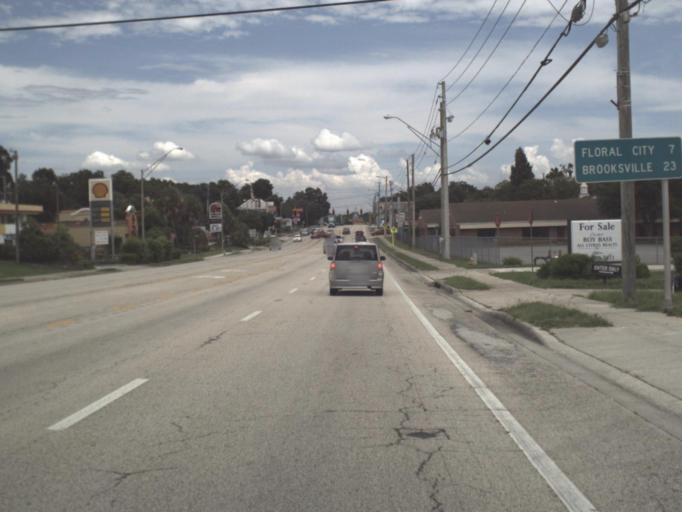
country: US
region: Florida
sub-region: Citrus County
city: Inverness
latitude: 28.8359
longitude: -82.3392
